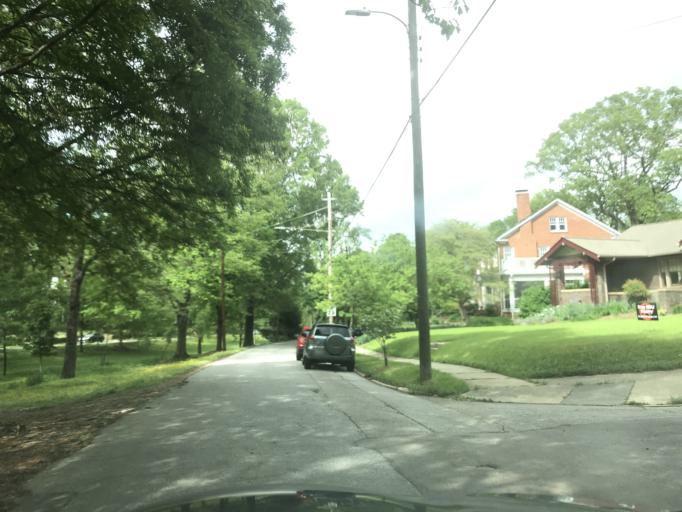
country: US
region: North Carolina
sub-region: Wake County
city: West Raleigh
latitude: 35.7842
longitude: -78.6551
